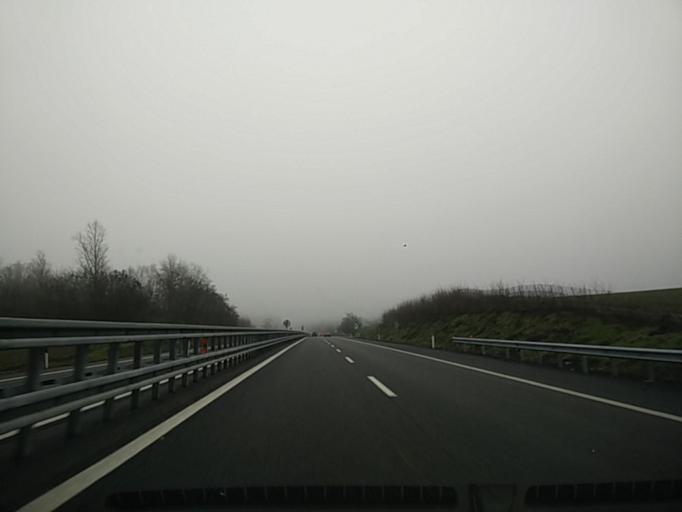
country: IT
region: Piedmont
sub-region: Provincia di Asti
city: Castello di Annone
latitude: 44.9103
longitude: 8.2988
